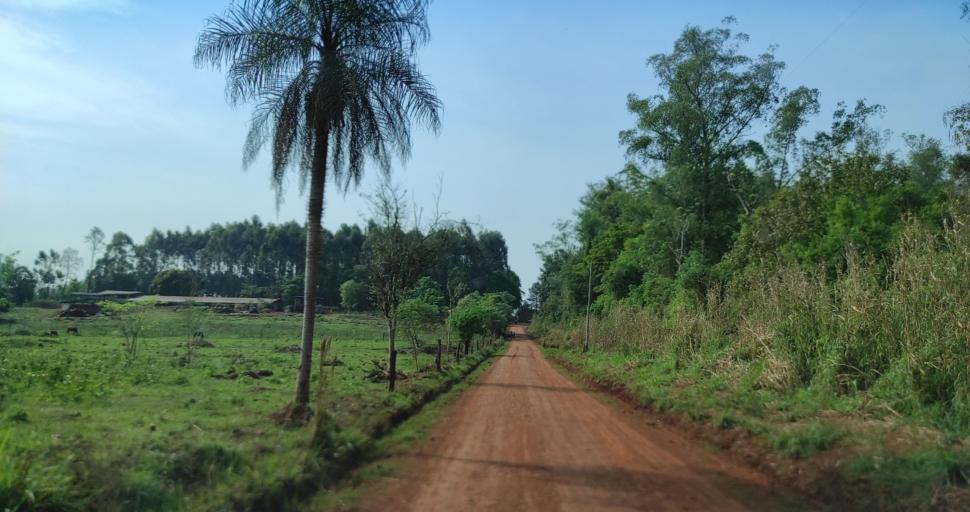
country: AR
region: Misiones
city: Capiovi
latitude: -26.8822
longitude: -55.0482
